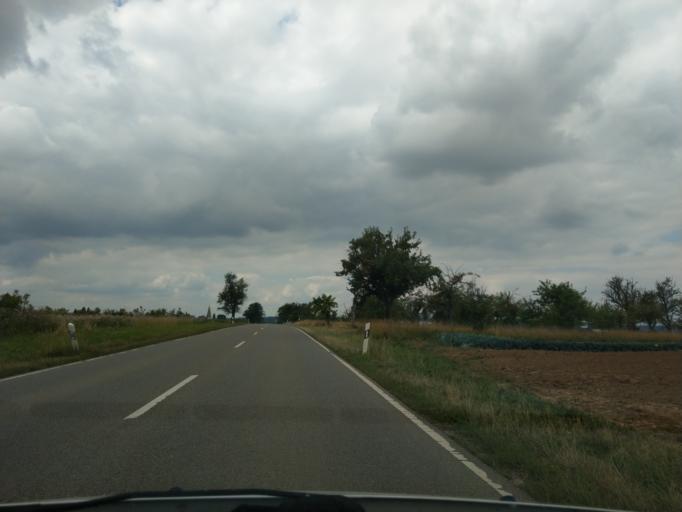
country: DE
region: Baden-Wuerttemberg
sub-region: Regierungsbezirk Stuttgart
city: Ostfildern
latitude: 48.6974
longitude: 9.2289
